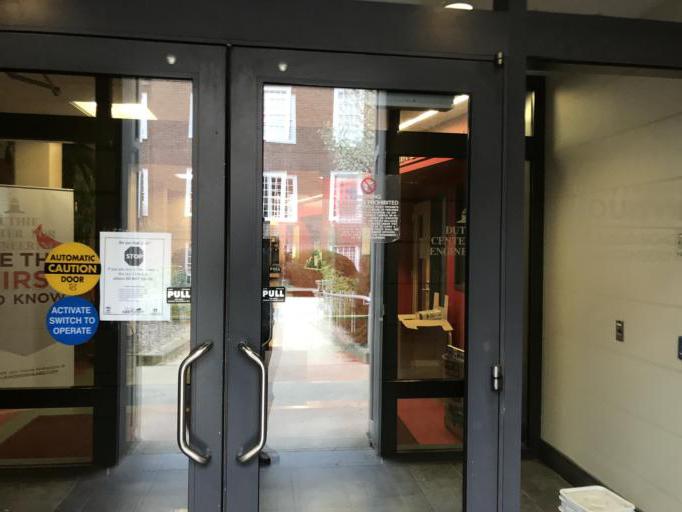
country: US
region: Kentucky
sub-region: Jefferson County
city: Audubon Park
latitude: 38.2130
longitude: -85.7608
